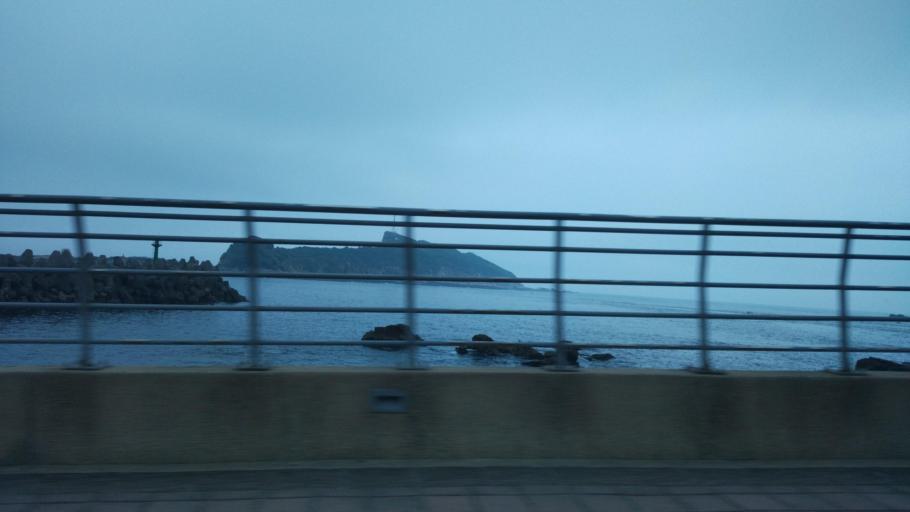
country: TW
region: Taiwan
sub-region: Keelung
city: Keelung
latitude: 25.2030
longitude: 121.6940
